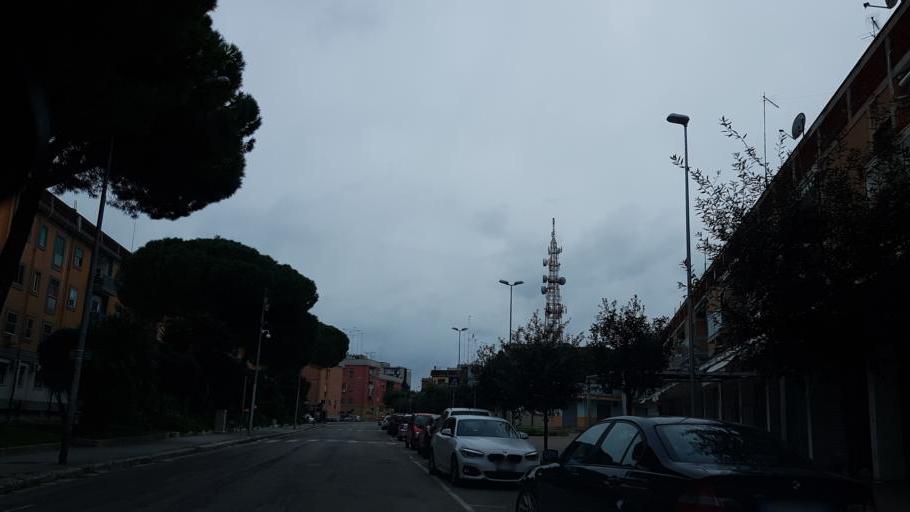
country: IT
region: Apulia
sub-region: Provincia di Brindisi
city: Brindisi
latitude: 40.6277
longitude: 17.9308
